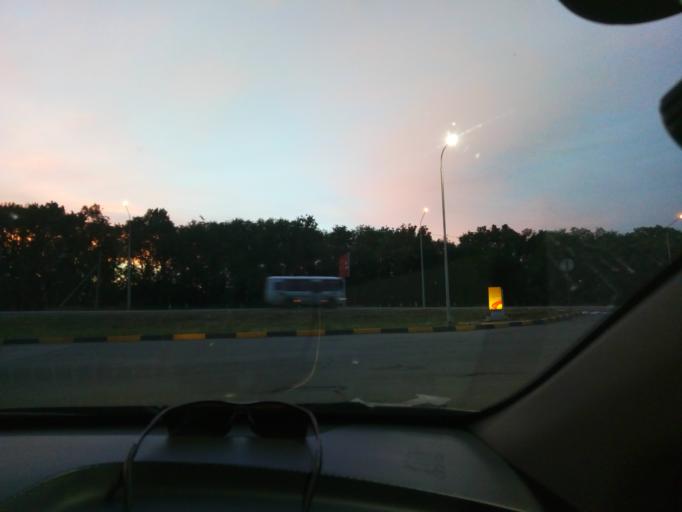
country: RU
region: Stavropol'skiy
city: Mikhaylovsk
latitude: 45.0618
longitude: 42.1230
